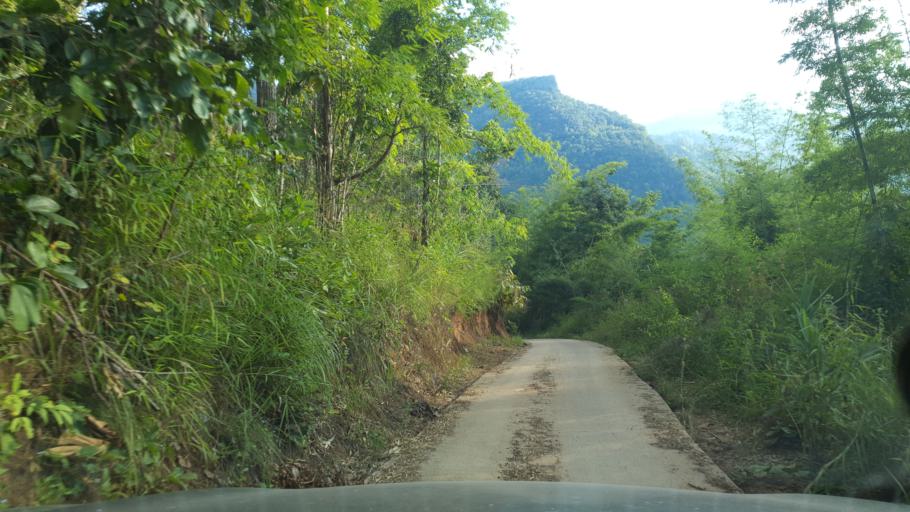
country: TH
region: Chiang Mai
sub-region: Amphoe Chiang Dao
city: Chiang Dao
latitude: 19.4091
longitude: 98.8324
